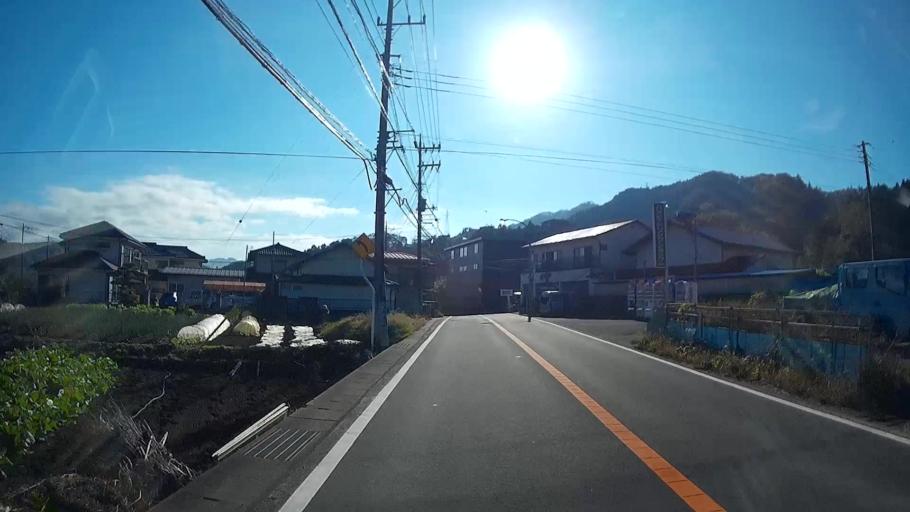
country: JP
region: Yamanashi
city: Uenohara
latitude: 35.6107
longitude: 139.1188
